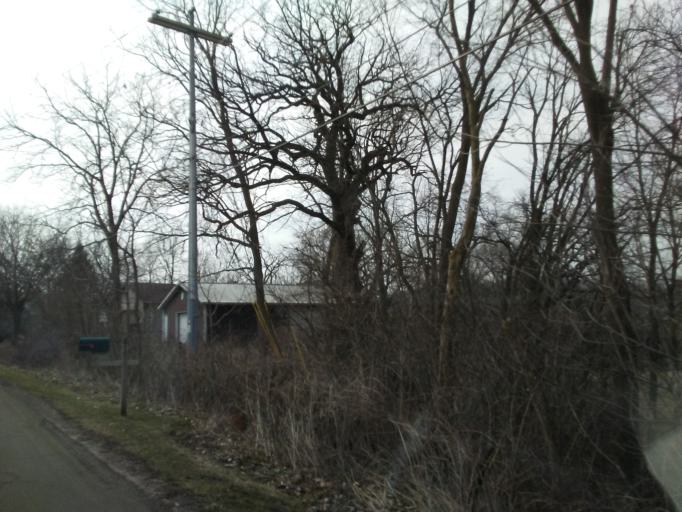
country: US
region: Wisconsin
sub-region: Columbia County
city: Lodi
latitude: 43.3243
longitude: -89.5317
